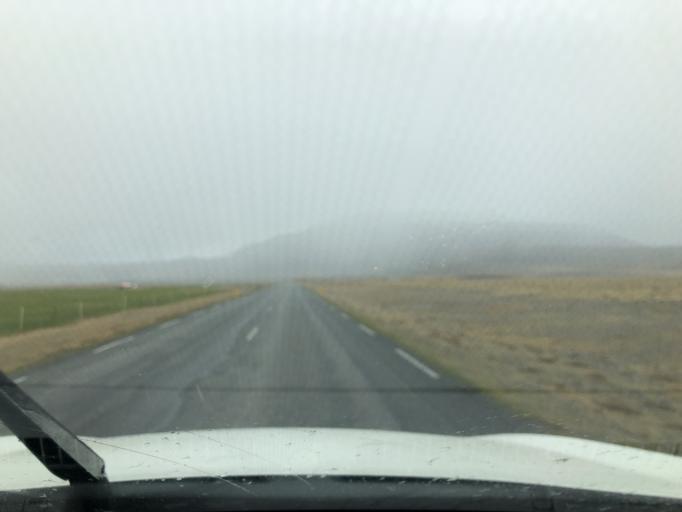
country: IS
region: East
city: Hoefn
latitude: 64.2527
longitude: -15.6247
